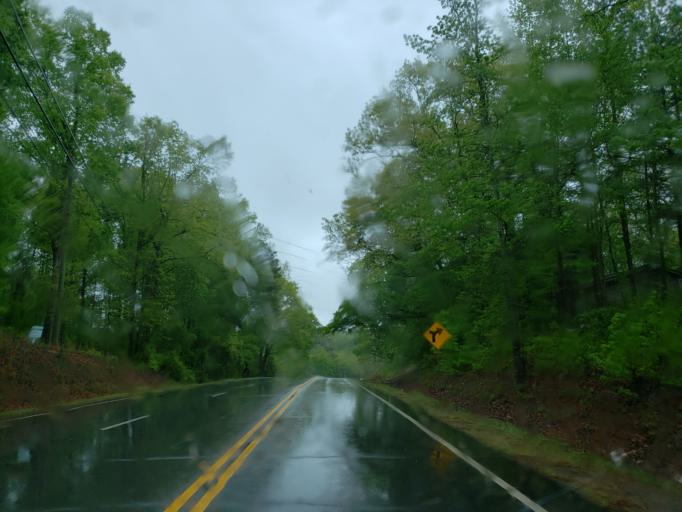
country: US
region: Georgia
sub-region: Carroll County
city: Temple
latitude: 33.7320
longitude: -85.0625
